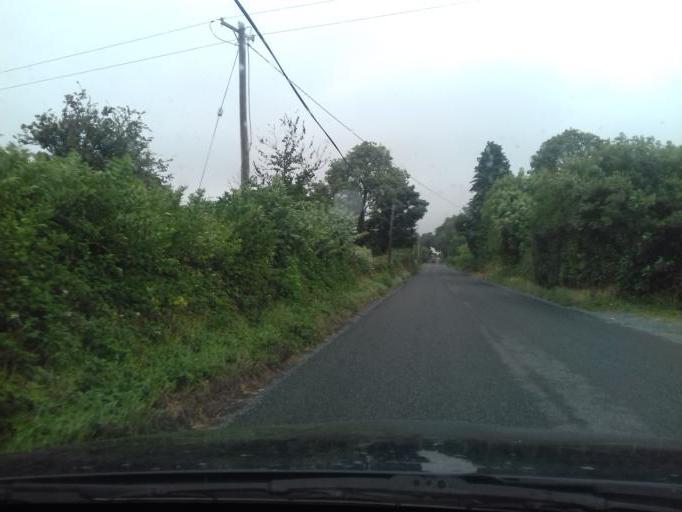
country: IE
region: Leinster
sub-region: Kilkenny
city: Graiguenamanagh
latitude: 52.6116
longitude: -6.9369
